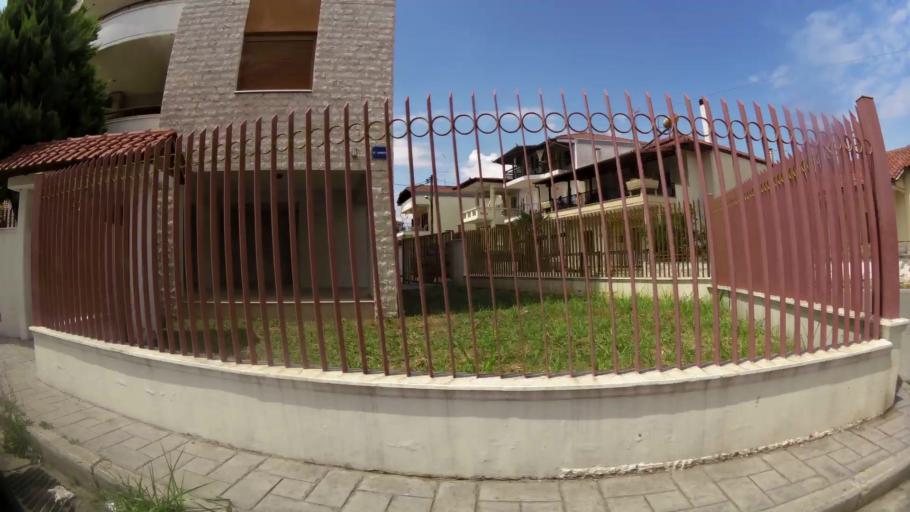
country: GR
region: Central Macedonia
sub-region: Nomos Pierias
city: Katerini
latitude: 40.2664
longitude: 22.5021
